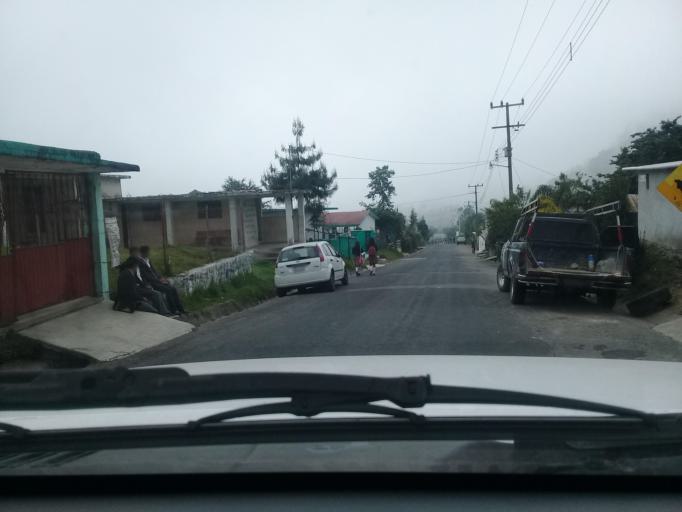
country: MX
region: Veracruz
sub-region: Mariano Escobedo
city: San Isidro el Berro
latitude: 18.9489
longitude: -97.2042
